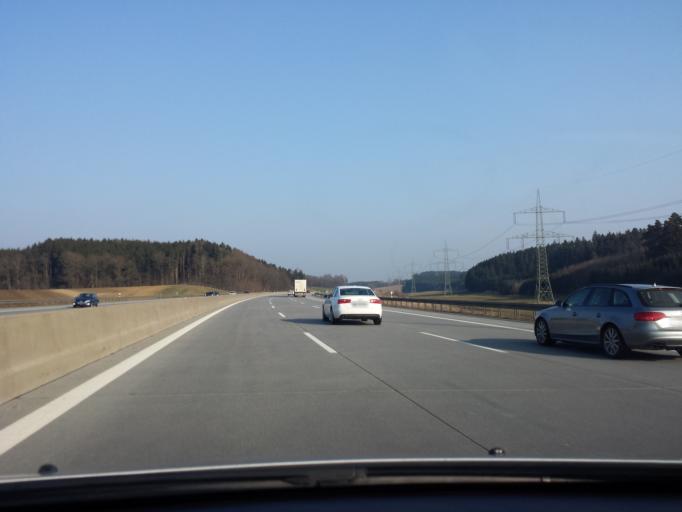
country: DE
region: Bavaria
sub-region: Swabia
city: Dasing
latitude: 48.3997
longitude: 11.0129
